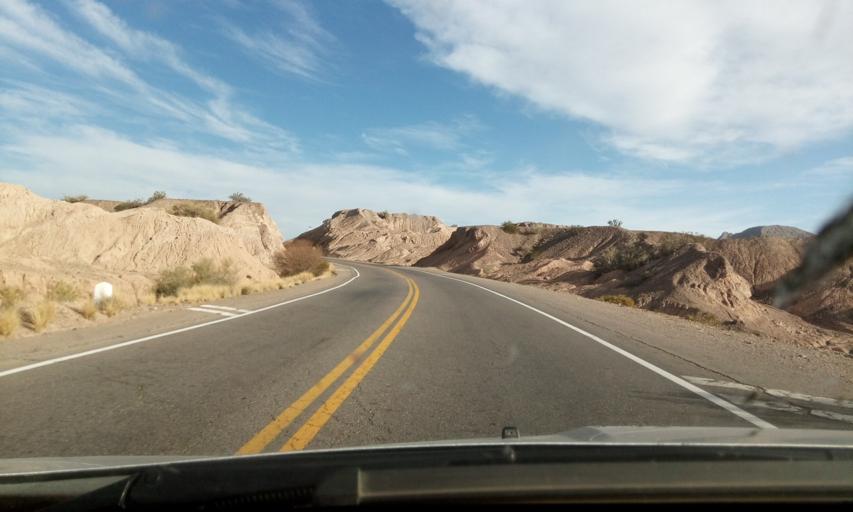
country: AR
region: San Juan
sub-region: Departamento de Rivadavia
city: Rivadavia
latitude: -31.4608
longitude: -68.6402
